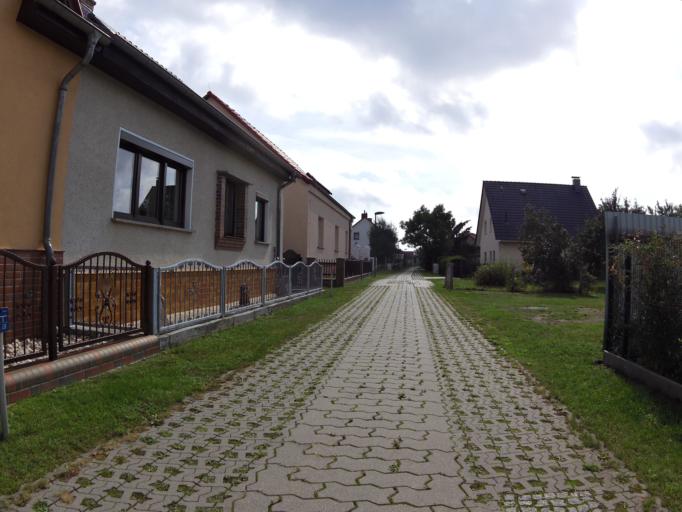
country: DE
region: Brandenburg
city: Storkow
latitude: 52.2777
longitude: 13.9295
